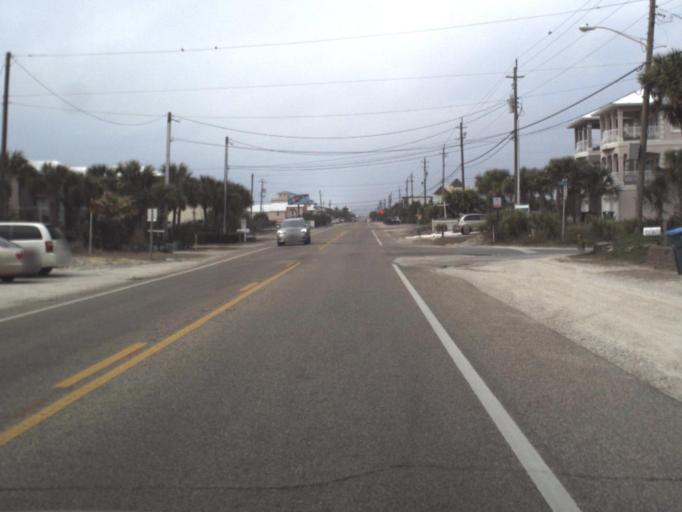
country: US
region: Florida
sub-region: Bay County
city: Laguna Beach
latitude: 30.2413
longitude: -85.9281
